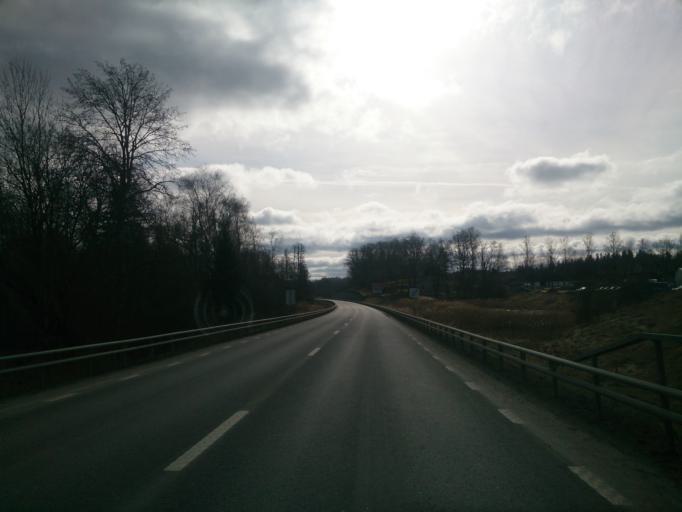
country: SE
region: OEstergoetland
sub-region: Atvidabergs Kommun
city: Atvidaberg
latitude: 58.1997
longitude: 16.0084
